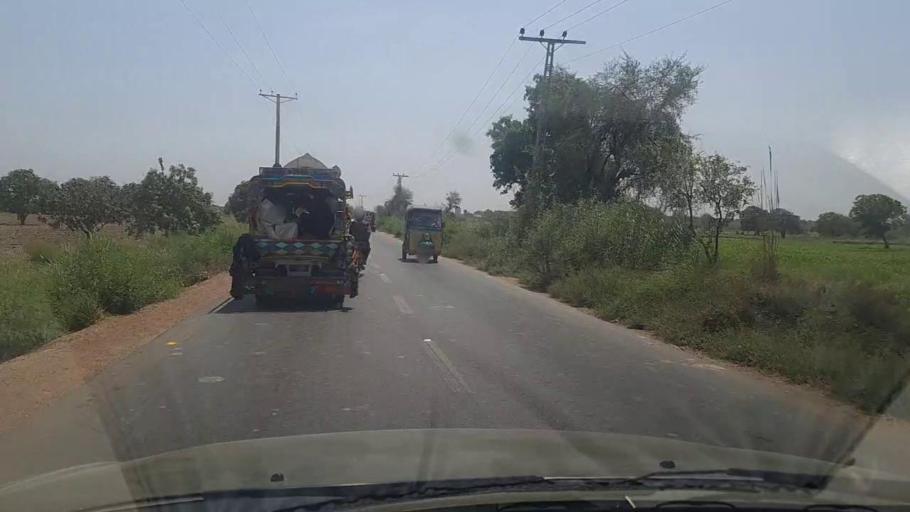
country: PK
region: Sindh
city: Hyderabad
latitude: 25.3907
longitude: 68.4095
